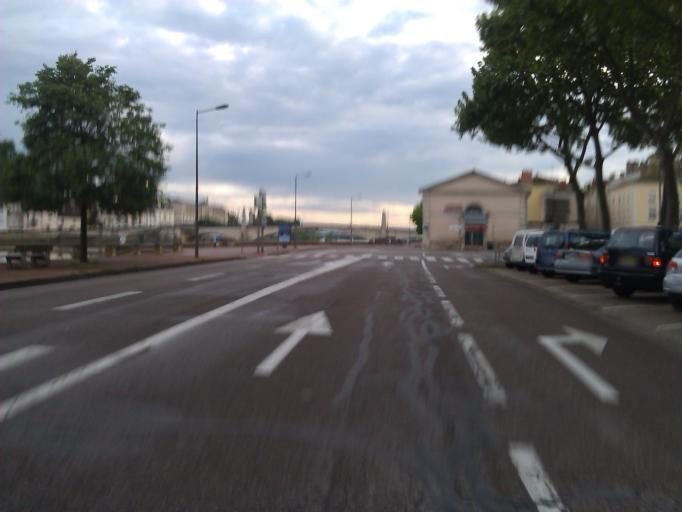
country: FR
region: Bourgogne
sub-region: Departement de Saone-et-Loire
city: Chalon-sur-Saone
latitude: 46.7822
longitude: 4.8620
